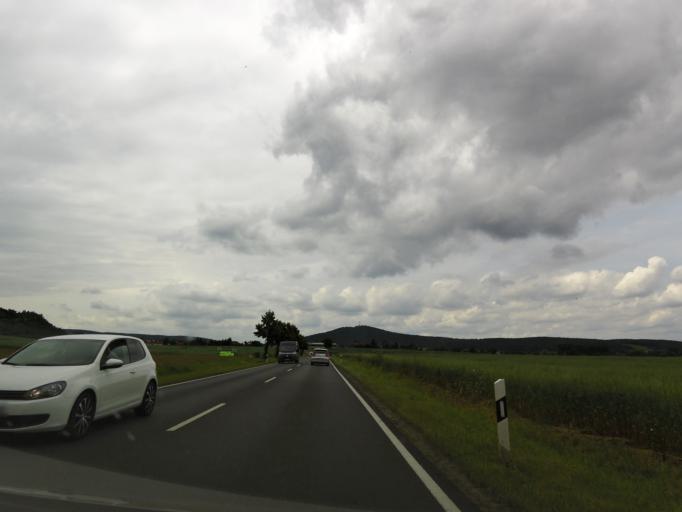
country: DE
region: Thuringia
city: Tiefenort
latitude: 50.8234
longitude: 10.1738
